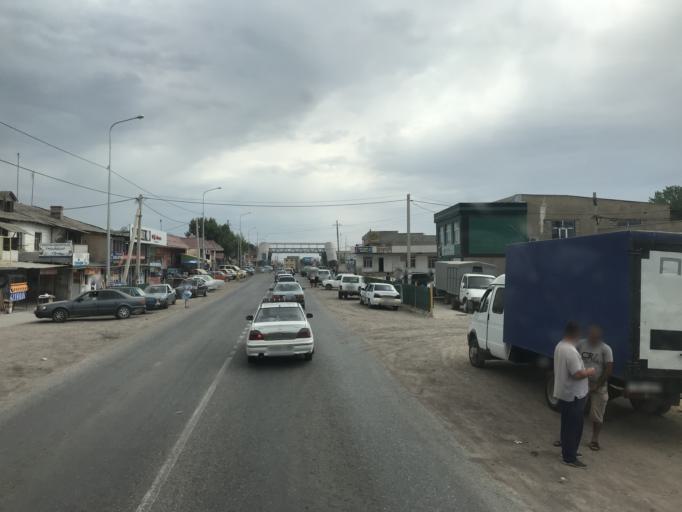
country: KZ
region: Ongtustik Qazaqstan
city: Saryaghash
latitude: 41.3410
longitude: 68.9530
